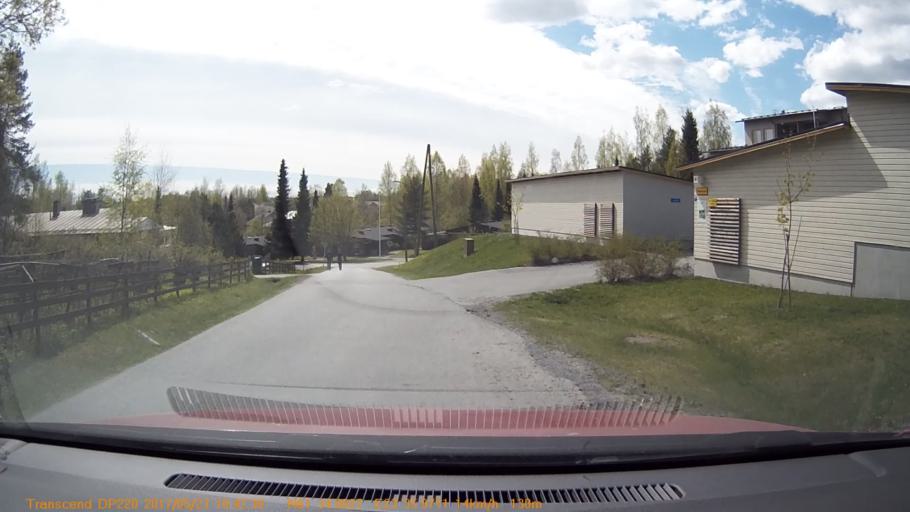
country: FI
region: Pirkanmaa
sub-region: Tampere
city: Yloejaervi
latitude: 61.5680
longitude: 23.5995
